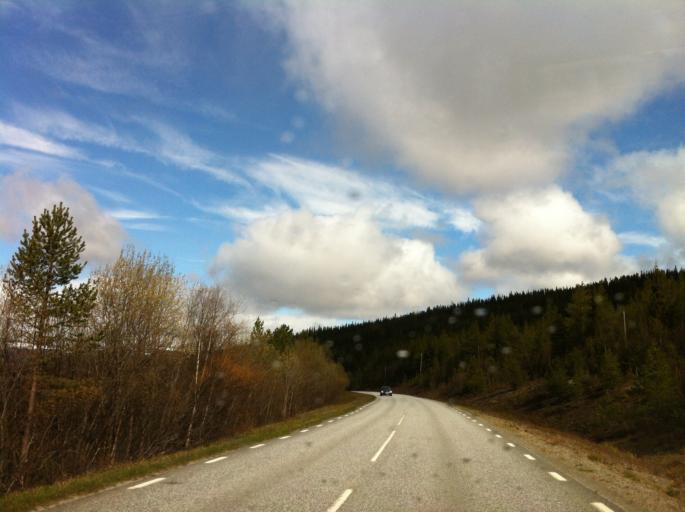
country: SE
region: Jaemtland
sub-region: Are Kommun
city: Are
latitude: 62.5796
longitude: 12.5592
